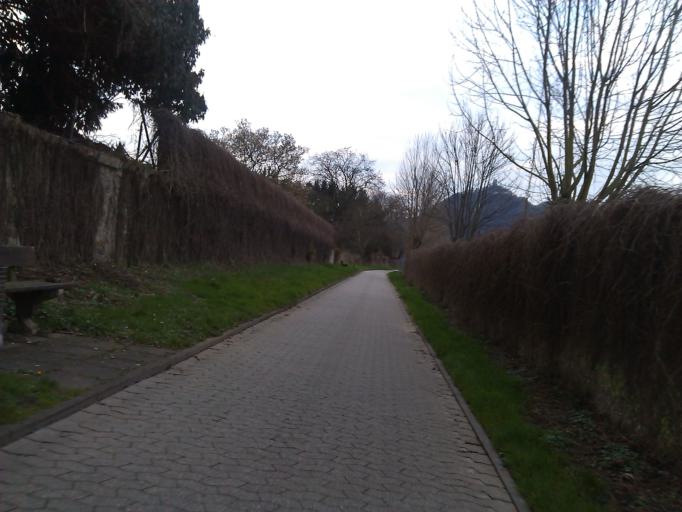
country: DE
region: North Rhine-Westphalia
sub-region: Regierungsbezirk Koln
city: Bad Honnef
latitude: 50.6467
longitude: 7.2064
